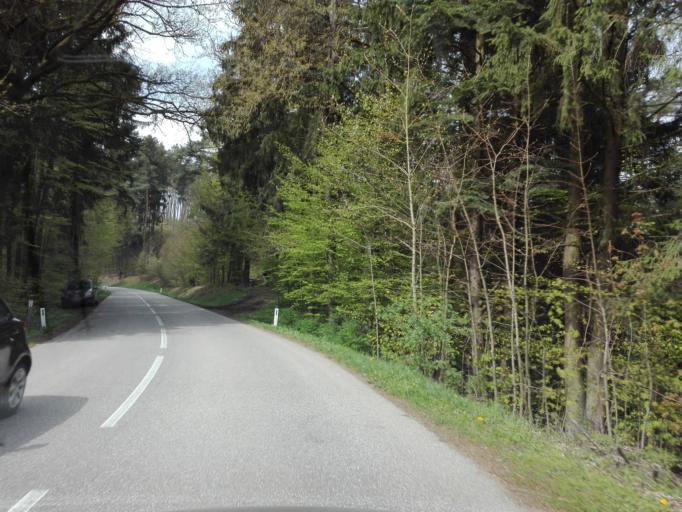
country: AT
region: Upper Austria
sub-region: Politischer Bezirk Urfahr-Umgebung
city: Walding
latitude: 48.3686
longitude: 14.1700
